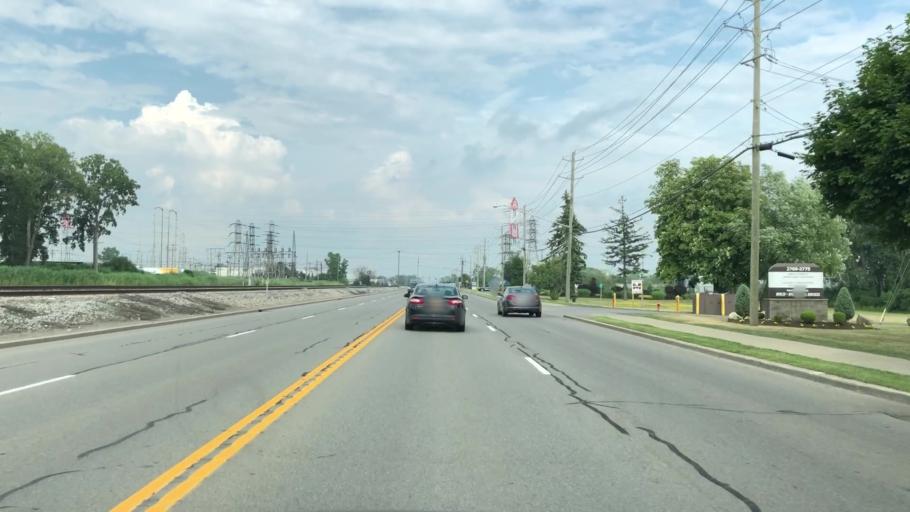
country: US
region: New York
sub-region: Erie County
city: Cheektowaga
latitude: 42.9019
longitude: -78.7721
